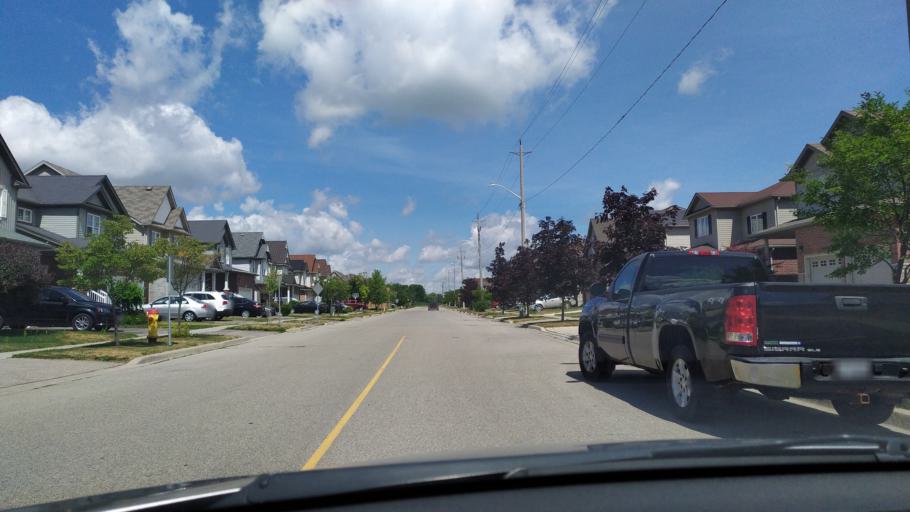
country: CA
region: Ontario
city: Kitchener
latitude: 43.4088
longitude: -80.6710
